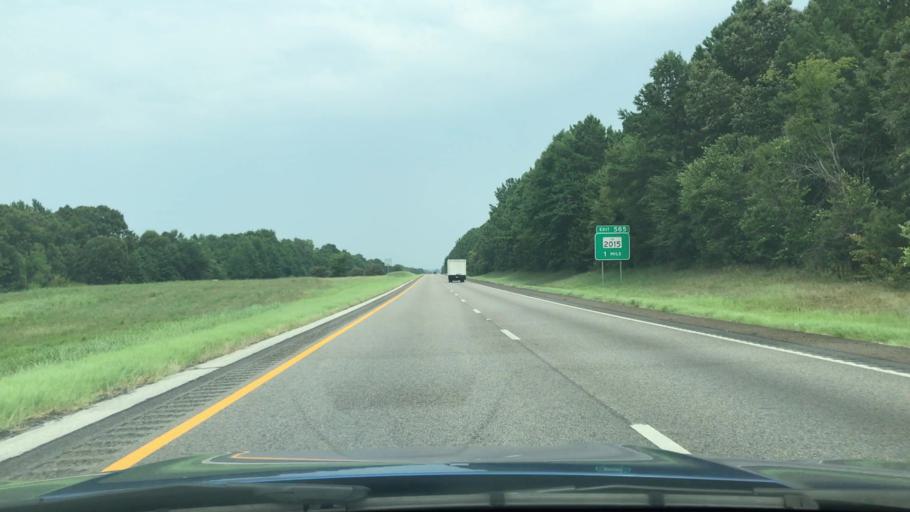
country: US
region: Texas
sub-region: Smith County
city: Tyler
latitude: 32.4521
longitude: -95.2534
